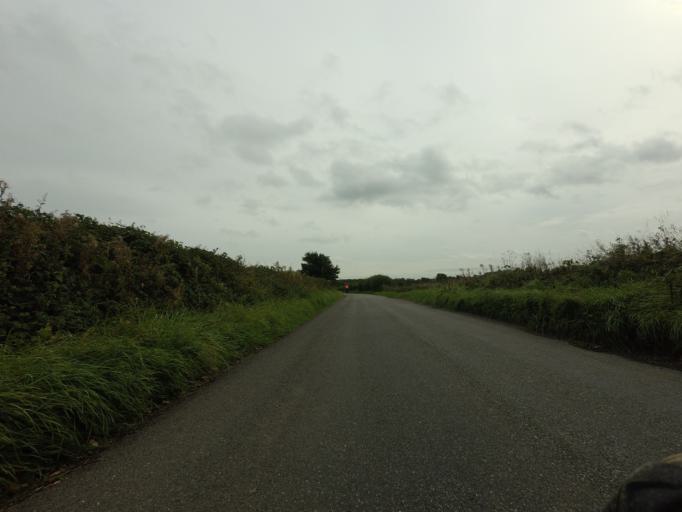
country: GB
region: England
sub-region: Hertfordshire
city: Buntingford
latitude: 51.9771
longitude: 0.0588
